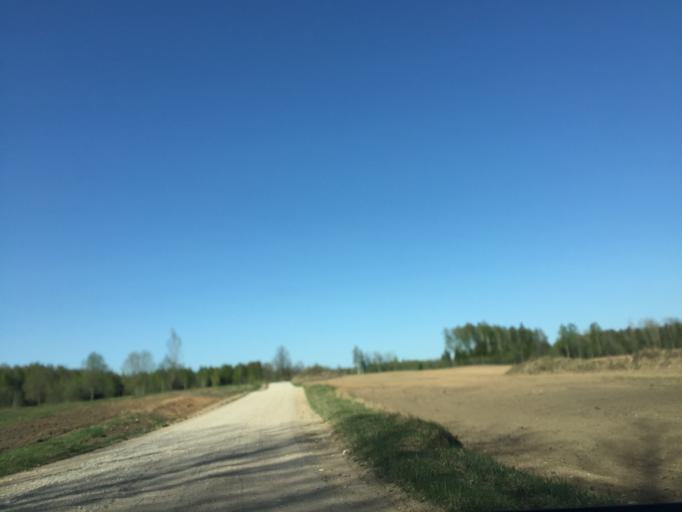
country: LV
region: Ergli
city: Ergli
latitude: 56.9160
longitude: 25.4510
